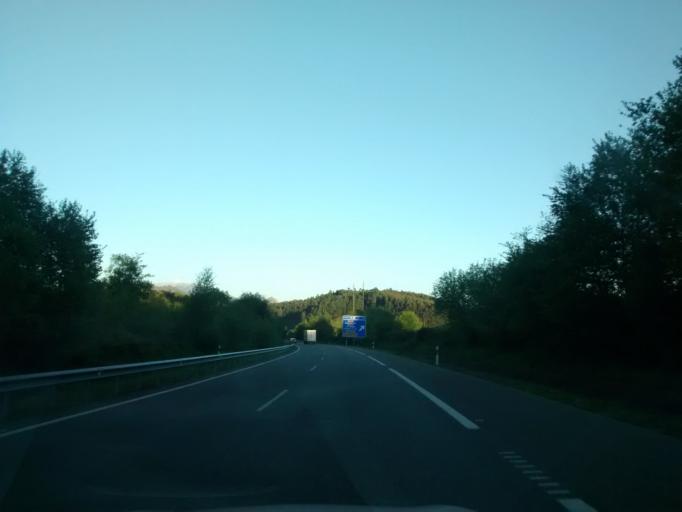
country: ES
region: Asturias
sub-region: Province of Asturias
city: Ribadesella
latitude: 43.4394
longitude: -5.0239
